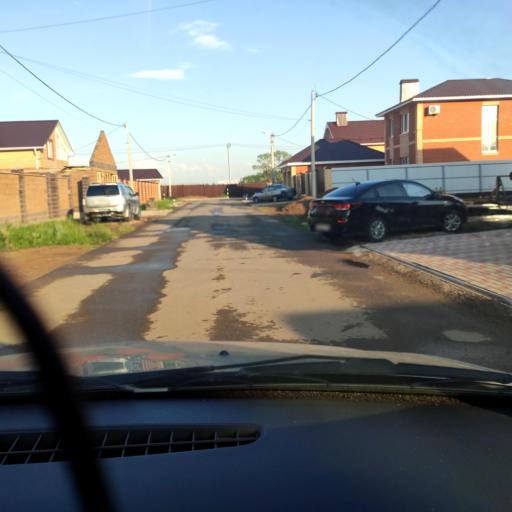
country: RU
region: Bashkortostan
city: Ufa
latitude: 54.6189
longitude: 55.8882
